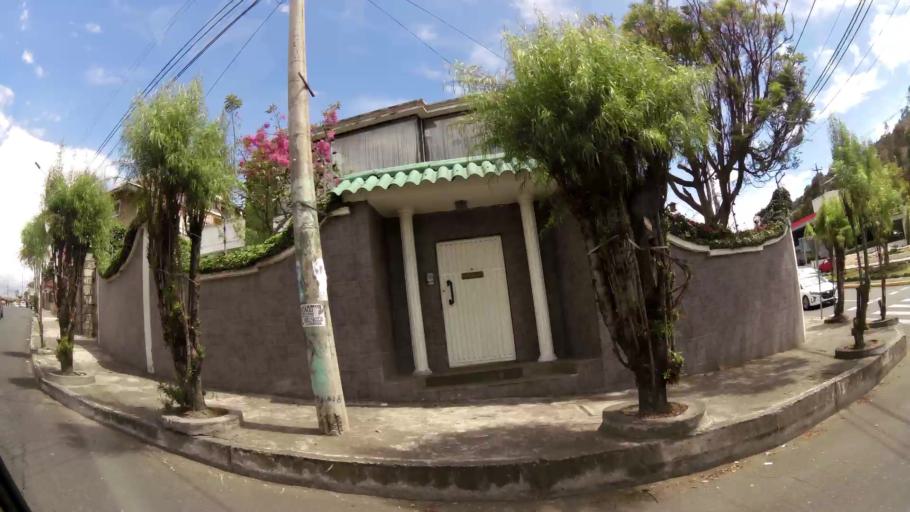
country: EC
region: Tungurahua
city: Ambato
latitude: -1.2568
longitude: -78.6413
